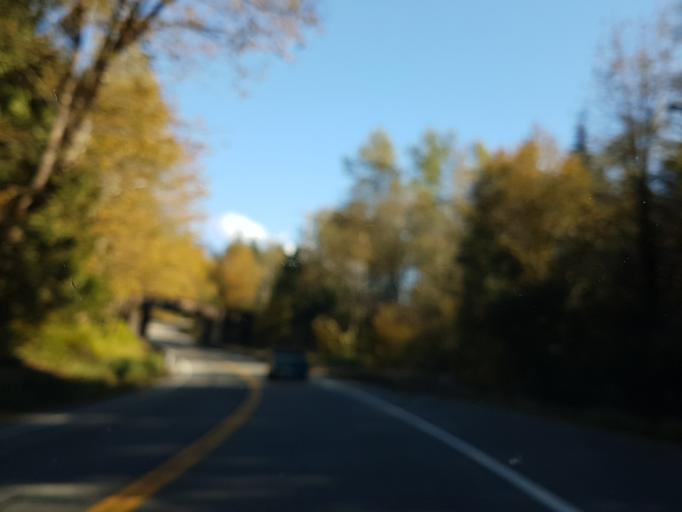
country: US
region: Washington
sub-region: Snohomish County
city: Gold Bar
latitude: 47.8107
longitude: -121.5678
